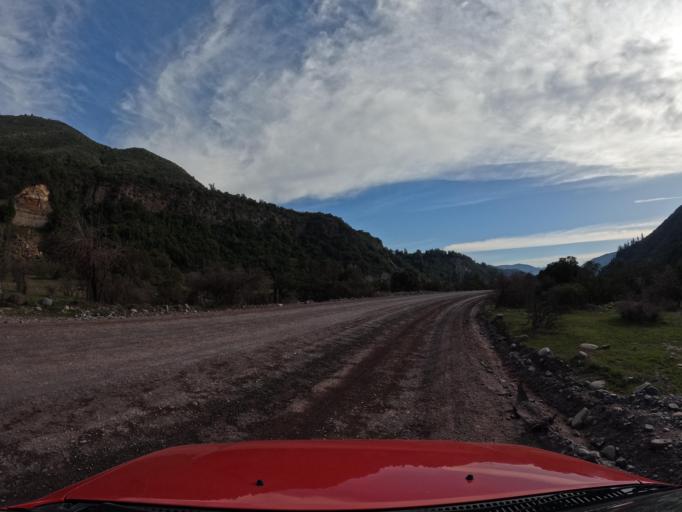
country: CL
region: O'Higgins
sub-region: Provincia de Colchagua
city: Chimbarongo
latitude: -34.9991
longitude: -70.7966
